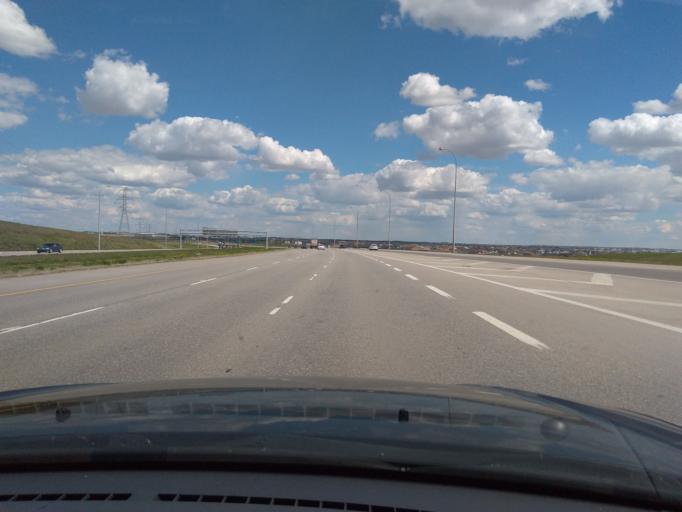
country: CA
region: Alberta
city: Calgary
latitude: 51.1728
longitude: -114.0637
